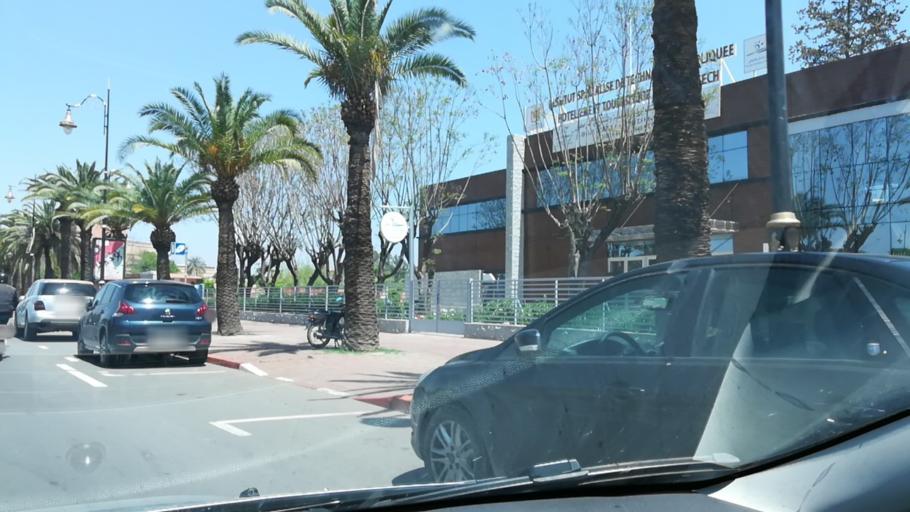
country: MA
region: Marrakech-Tensift-Al Haouz
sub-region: Marrakech
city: Marrakesh
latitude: 31.6263
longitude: -8.0134
